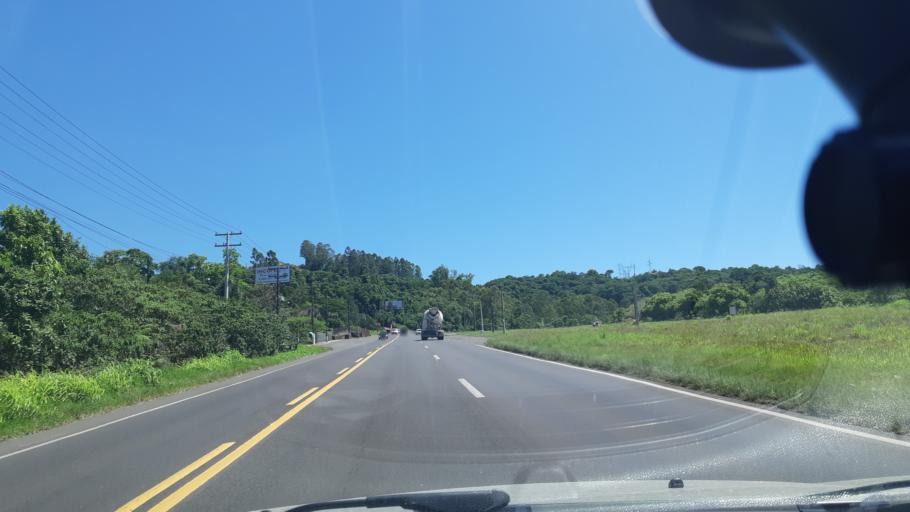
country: BR
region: Rio Grande do Sul
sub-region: Estancia Velha
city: Estancia Velha
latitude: -29.6350
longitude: -51.1426
